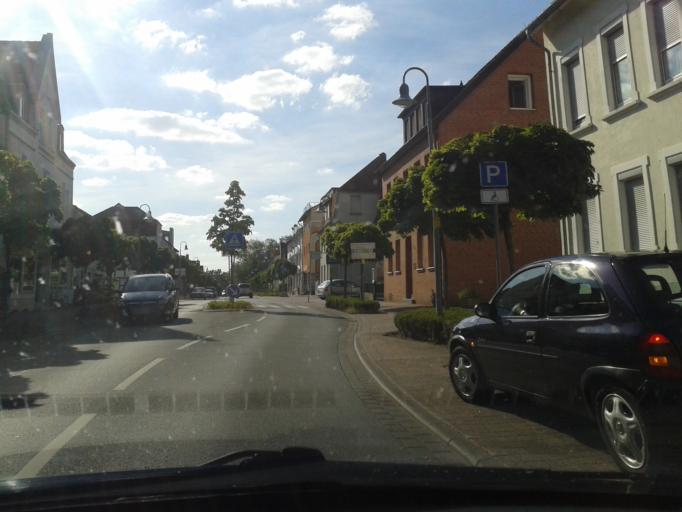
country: DE
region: North Rhine-Westphalia
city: Bad Lippspringe
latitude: 51.7827
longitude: 8.8169
